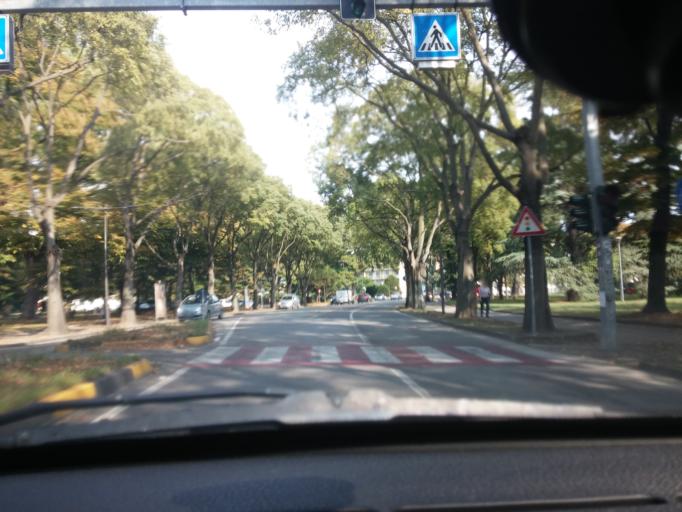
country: IT
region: Emilia-Romagna
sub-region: Provincia di Ferrara
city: Ferrara
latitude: 44.8437
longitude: 11.6064
